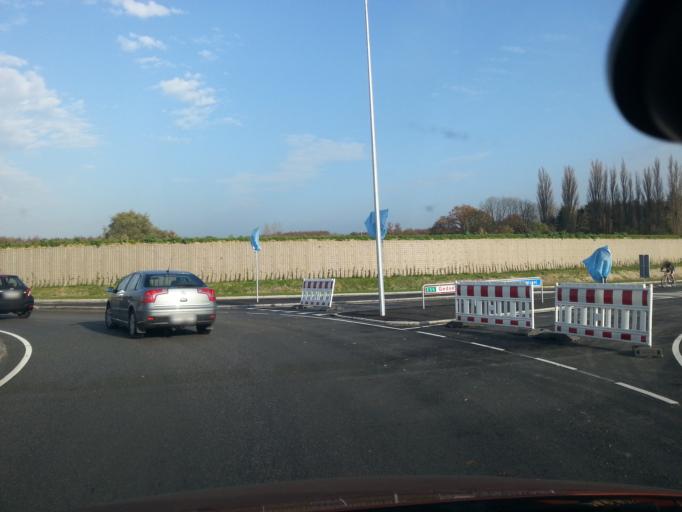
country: DK
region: Zealand
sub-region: Guldborgsund Kommune
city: Nykobing Falster
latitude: 54.7829
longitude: 11.8820
